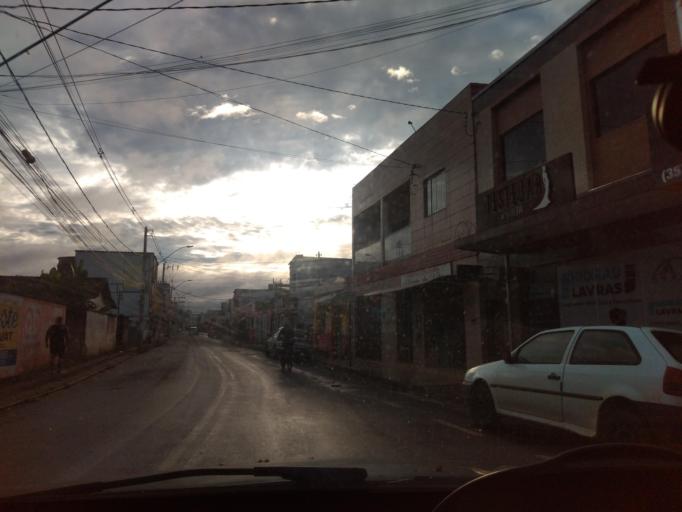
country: BR
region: Minas Gerais
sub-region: Lavras
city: Lavras
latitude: -21.2474
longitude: -45.0102
